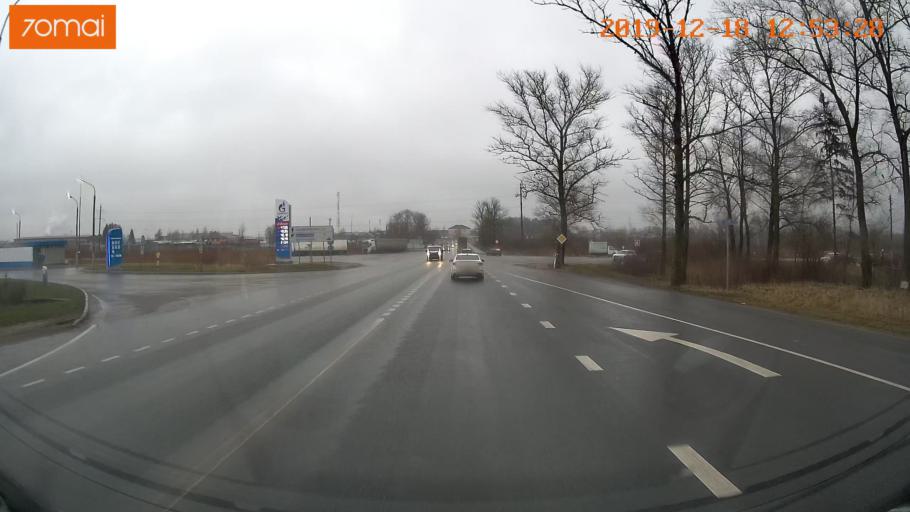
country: RU
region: Moskovskaya
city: Klin
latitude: 56.3193
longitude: 36.6945
